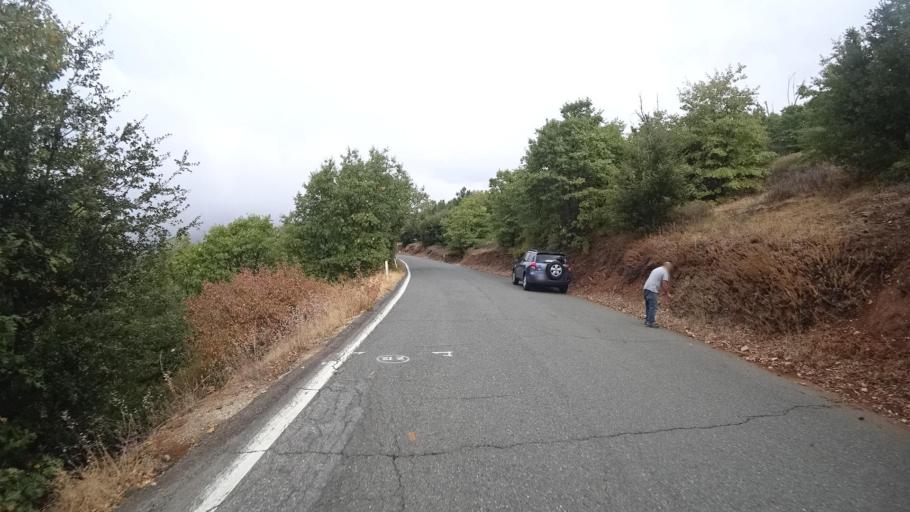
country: US
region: California
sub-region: San Diego County
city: Julian
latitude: 33.0058
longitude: -116.6039
